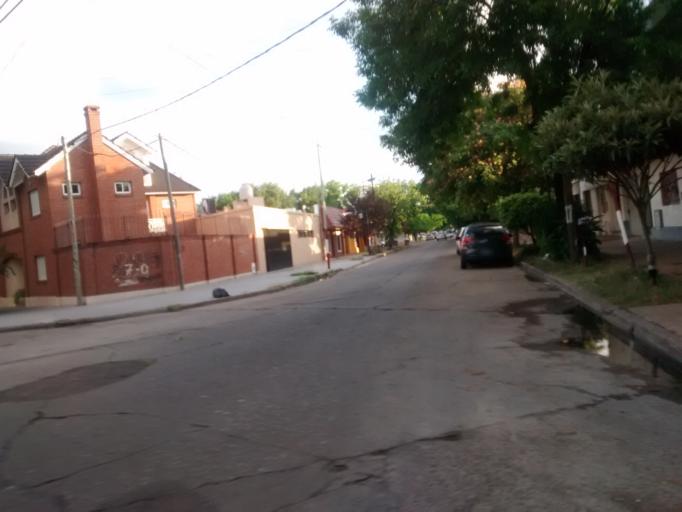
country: AR
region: Buenos Aires
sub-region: Partido de La Plata
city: La Plata
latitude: -34.9185
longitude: -57.9673
